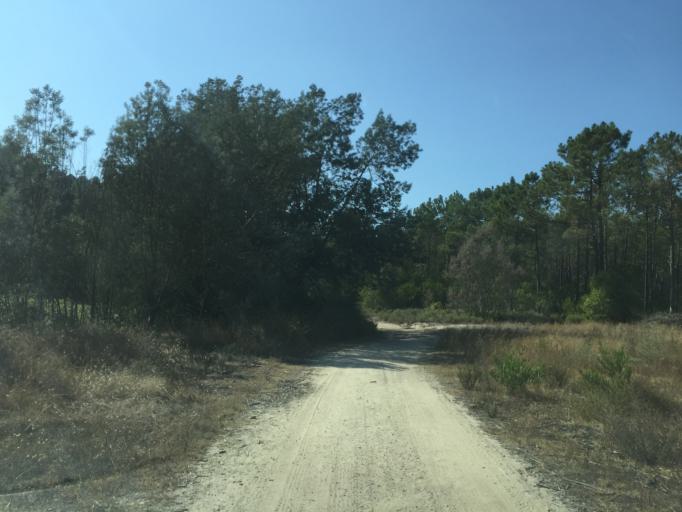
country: PT
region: Coimbra
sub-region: Figueira da Foz
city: Tavarede
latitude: 40.2279
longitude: -8.8522
